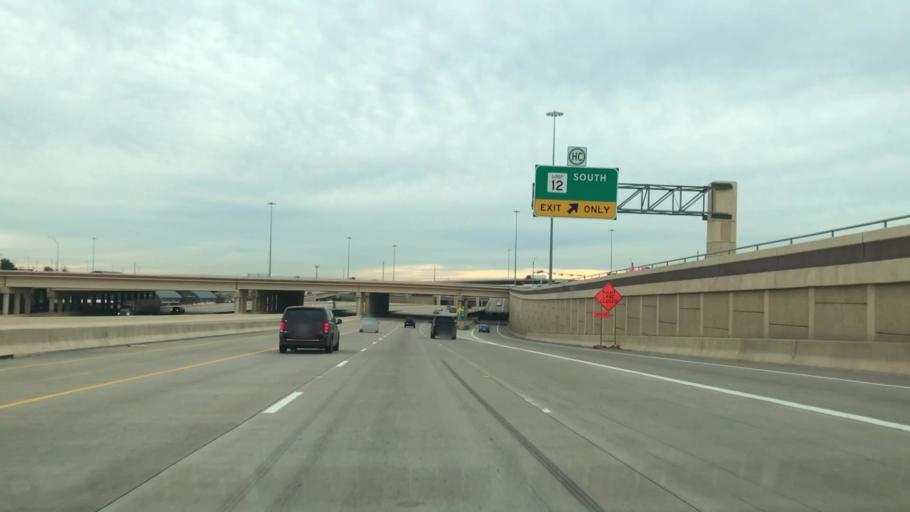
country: US
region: Texas
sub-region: Dallas County
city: Irving
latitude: 32.8498
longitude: -96.9184
